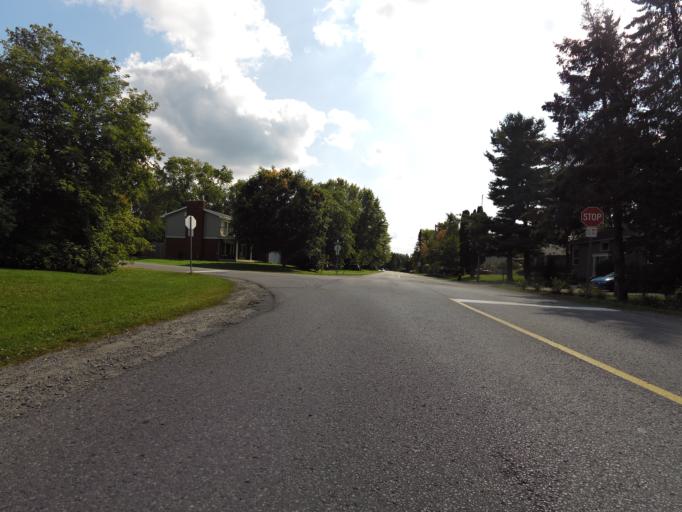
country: CA
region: Ontario
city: Bells Corners
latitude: 45.2405
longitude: -75.7012
